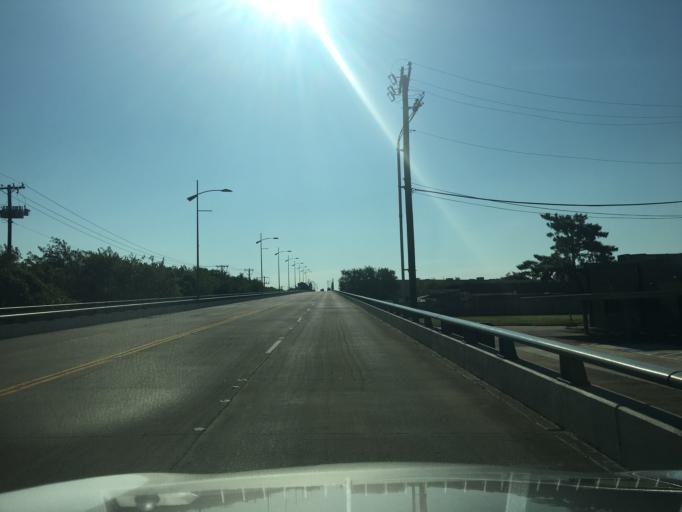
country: US
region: Texas
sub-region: Dallas County
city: Addison
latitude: 32.9563
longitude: -96.8431
